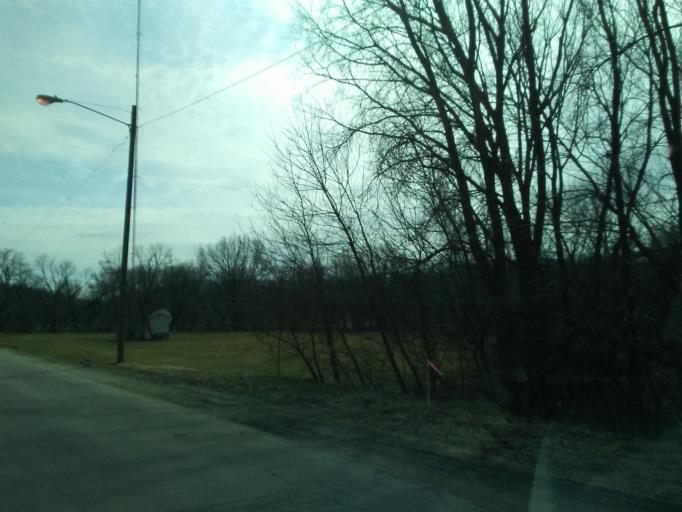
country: US
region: Iowa
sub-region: Winneshiek County
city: Decorah
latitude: 43.3105
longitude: -91.8087
